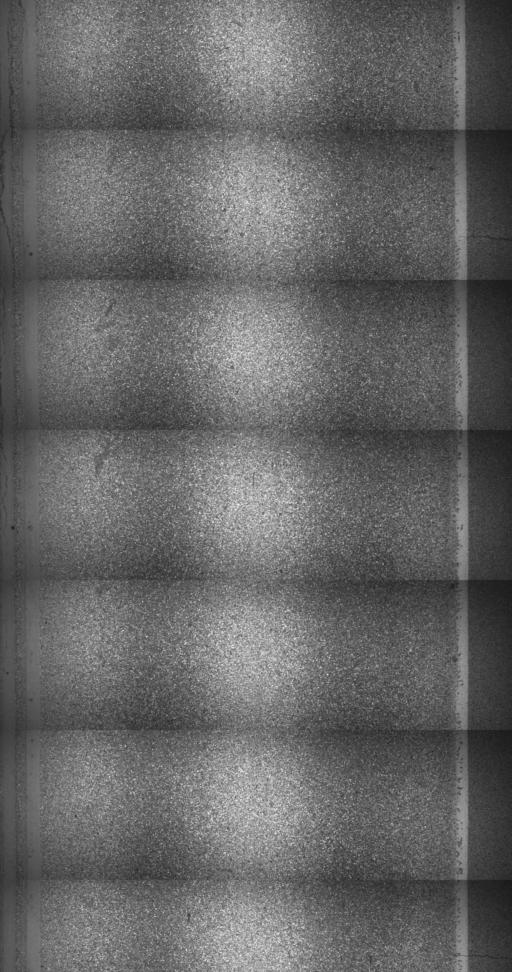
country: US
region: Vermont
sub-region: Lamoille County
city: Johnson
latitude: 44.6566
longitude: -72.7689
